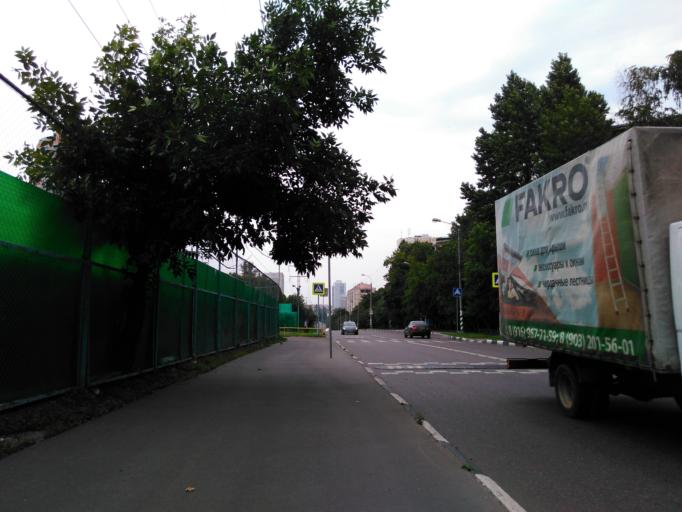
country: RU
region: Moskovskaya
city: Semenovskoye
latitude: 55.6751
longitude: 37.5480
